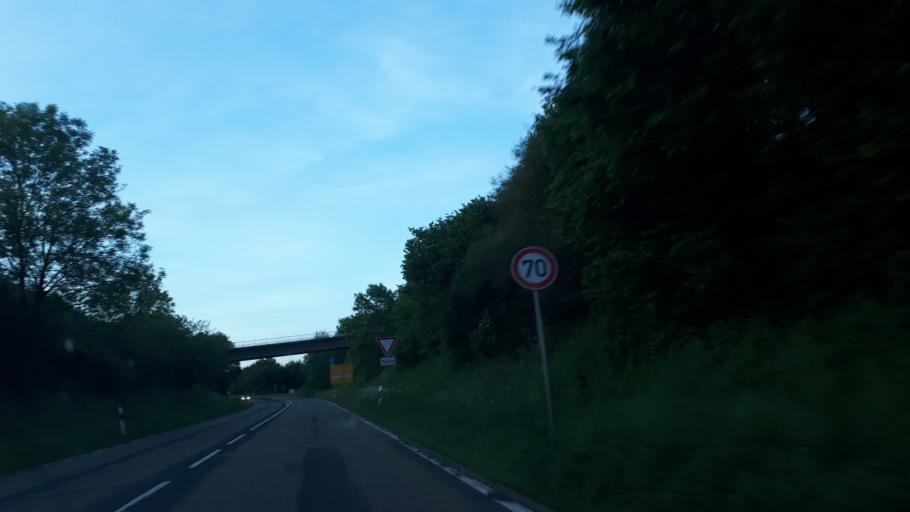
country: DE
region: Rheinland-Pfalz
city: Kaisersesch
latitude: 50.2317
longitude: 7.1463
